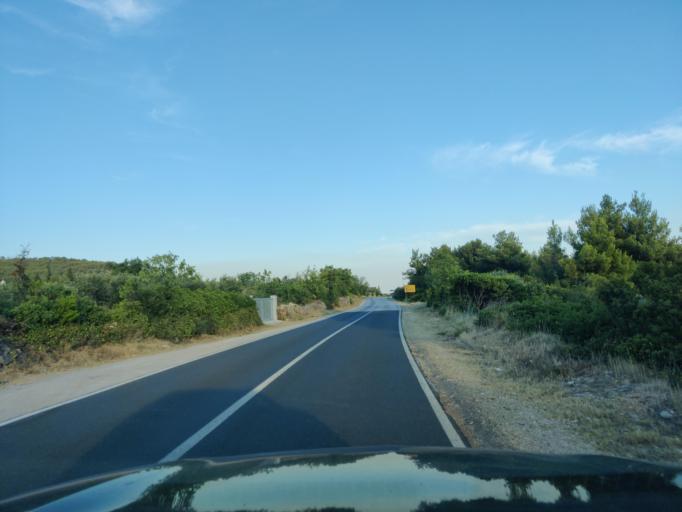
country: HR
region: Sibensko-Kniniska
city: Tribunj
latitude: 43.7656
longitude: 15.7356
